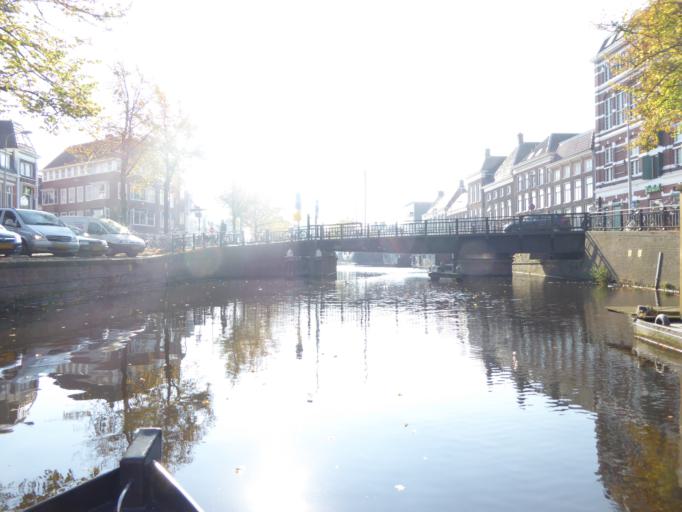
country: NL
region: Groningen
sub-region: Gemeente Groningen
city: Groningen
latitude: 53.2189
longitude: 6.5726
